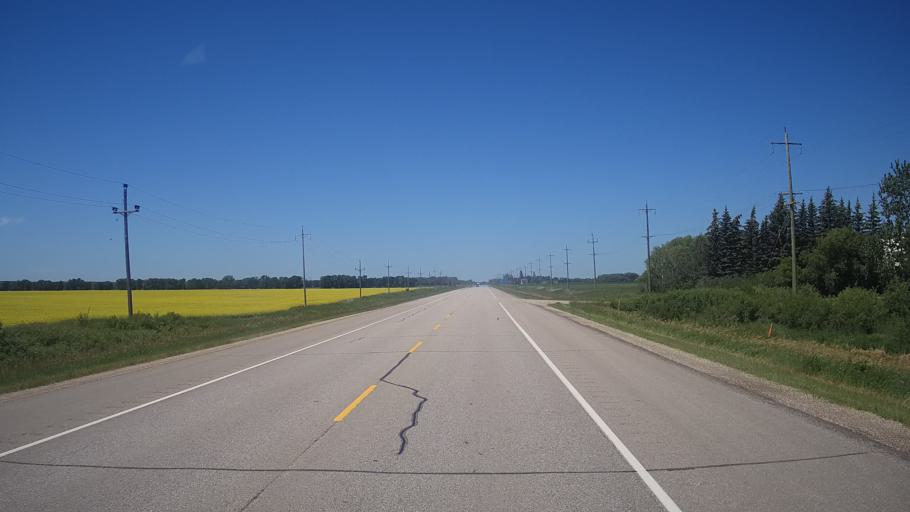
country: CA
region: Manitoba
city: Neepawa
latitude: 50.2253
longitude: -99.3201
